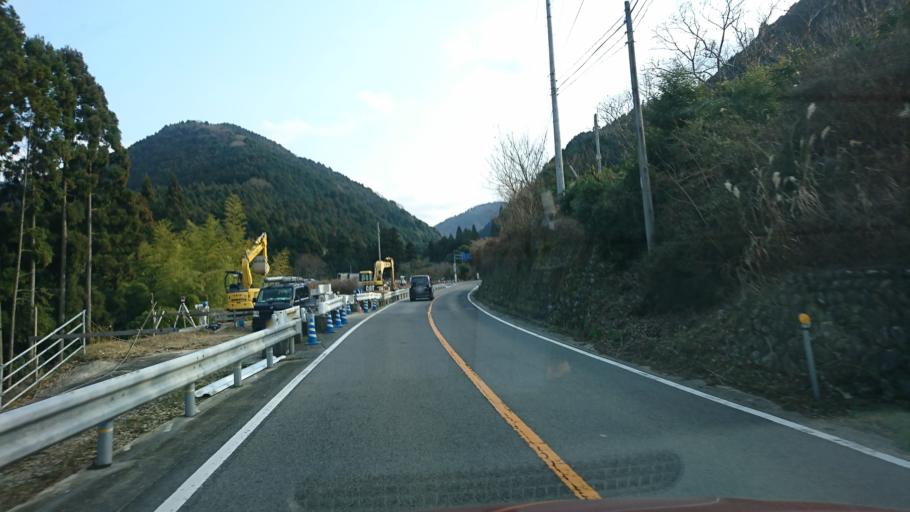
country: JP
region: Ehime
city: Hojo
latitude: 33.9685
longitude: 132.9042
